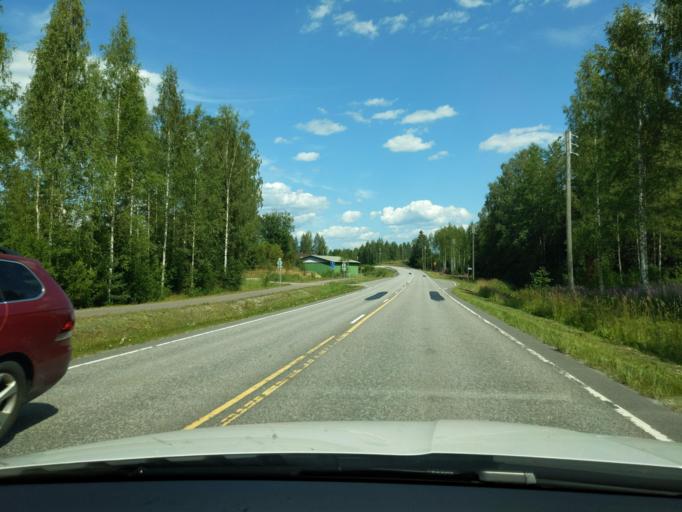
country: FI
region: Paijanne Tavastia
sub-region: Lahti
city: Heinola
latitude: 61.1120
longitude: 25.9421
